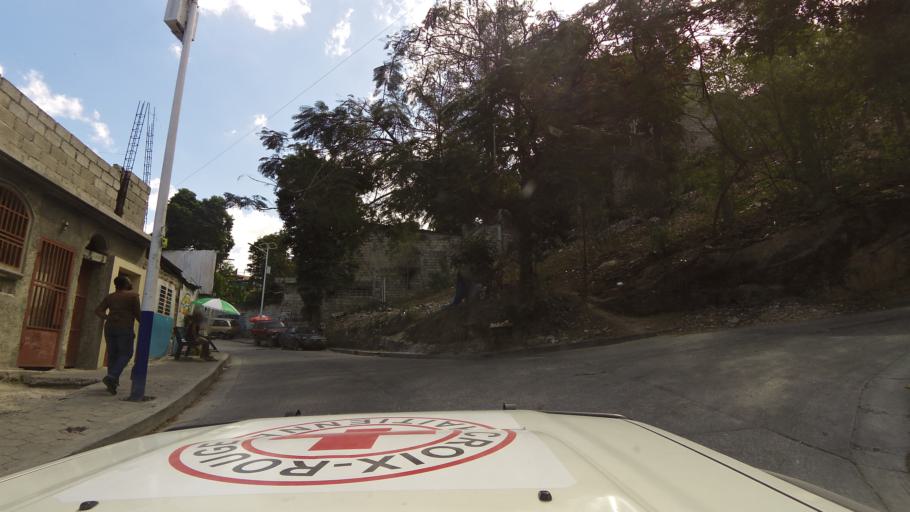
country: HT
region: Ouest
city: Petionville
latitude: 18.5270
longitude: -72.2919
